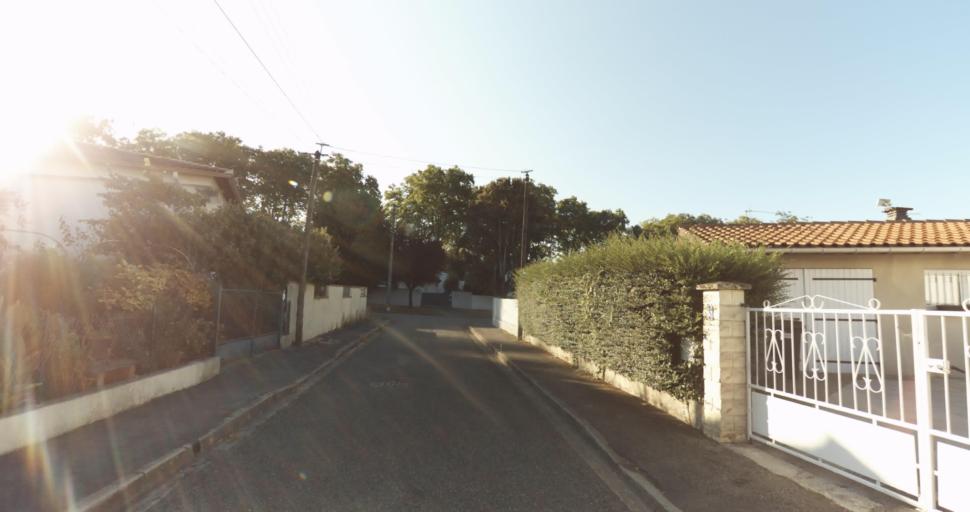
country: FR
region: Midi-Pyrenees
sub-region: Departement de la Haute-Garonne
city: L'Union
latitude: 43.6539
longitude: 1.4736
